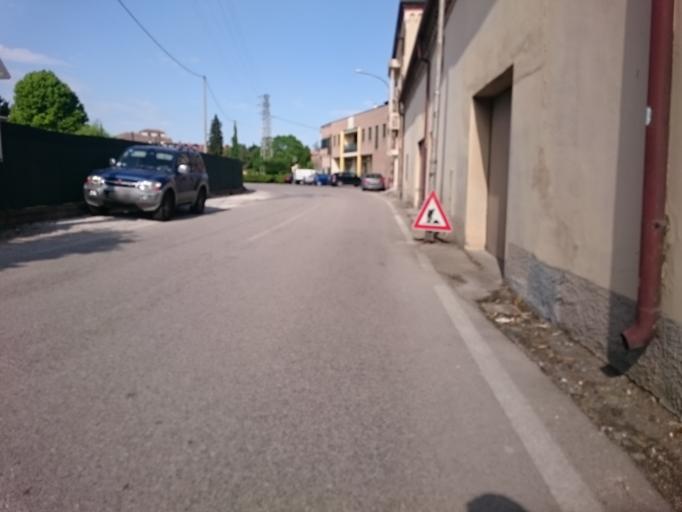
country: IT
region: Veneto
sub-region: Provincia di Padova
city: Montagnana
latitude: 45.2287
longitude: 11.4682
